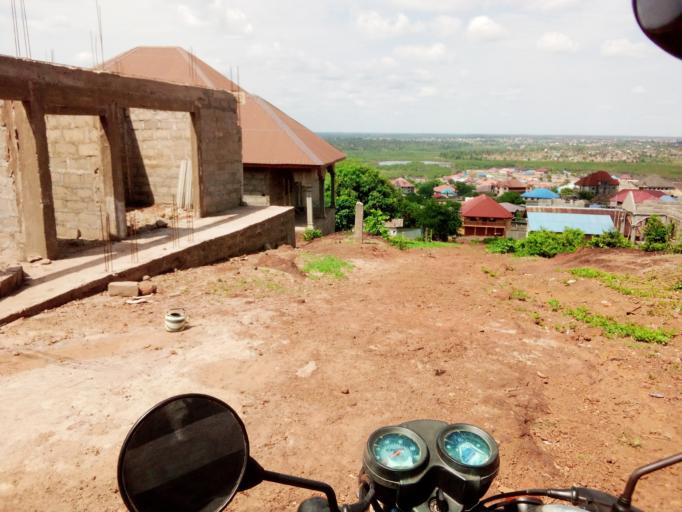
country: SL
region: Western Area
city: Waterloo
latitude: 8.3507
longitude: -13.0803
